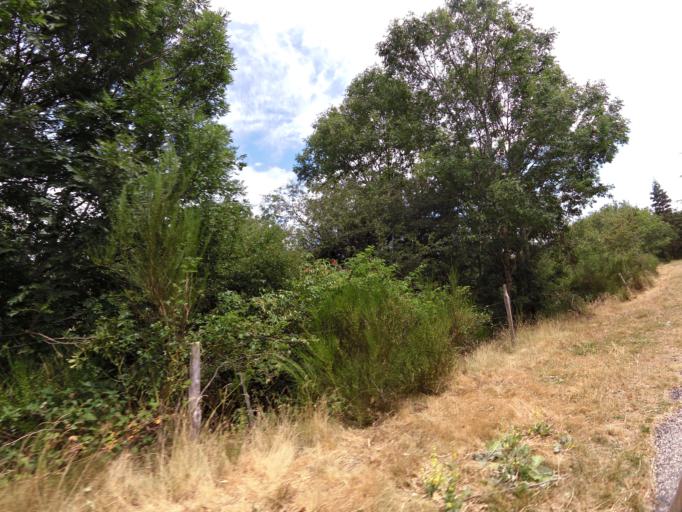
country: FR
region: Languedoc-Roussillon
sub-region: Departement du Gard
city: Valleraugue
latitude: 44.0390
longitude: 3.6063
